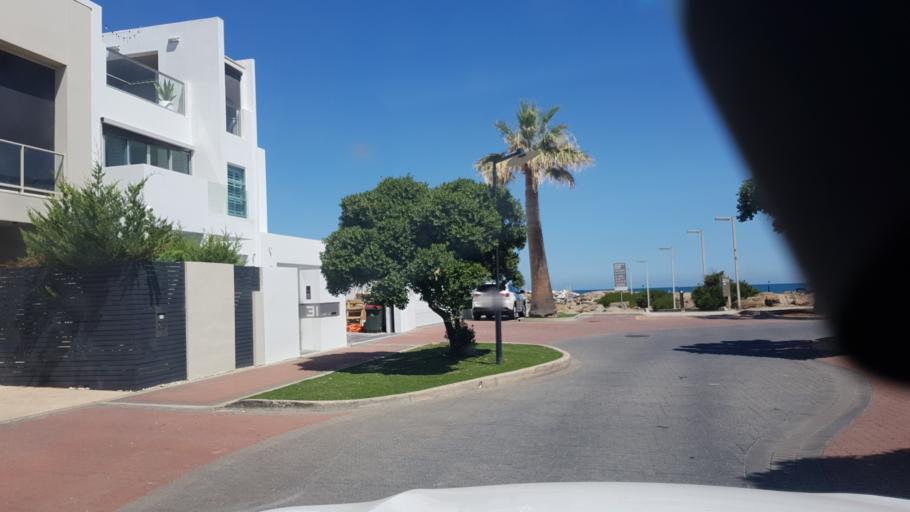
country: AU
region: South Australia
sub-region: Adelaide
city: Glenelg
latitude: -34.9744
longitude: 138.5114
